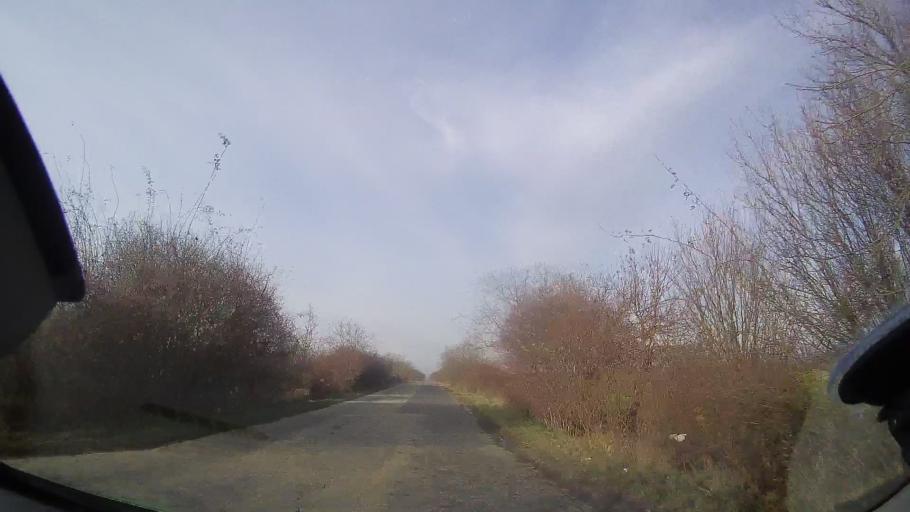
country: RO
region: Bihor
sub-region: Comuna Spinus
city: Spinus
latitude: 47.2151
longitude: 22.1760
